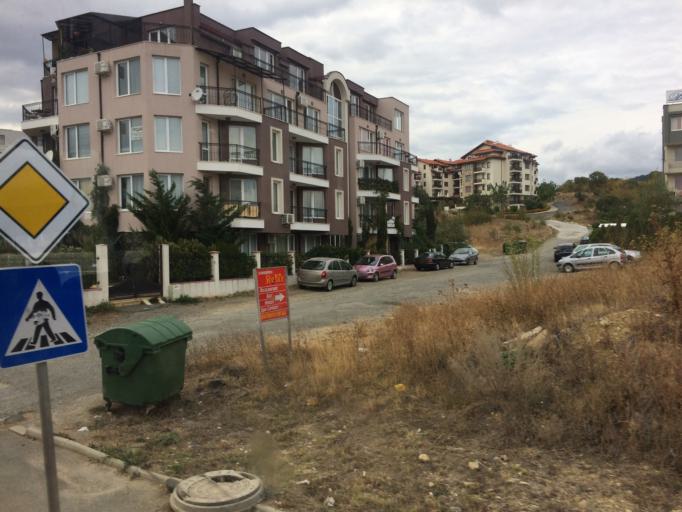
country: BG
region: Burgas
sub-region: Obshtina Nesebur
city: Sveti Vlas
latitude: 42.7122
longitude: 27.7396
